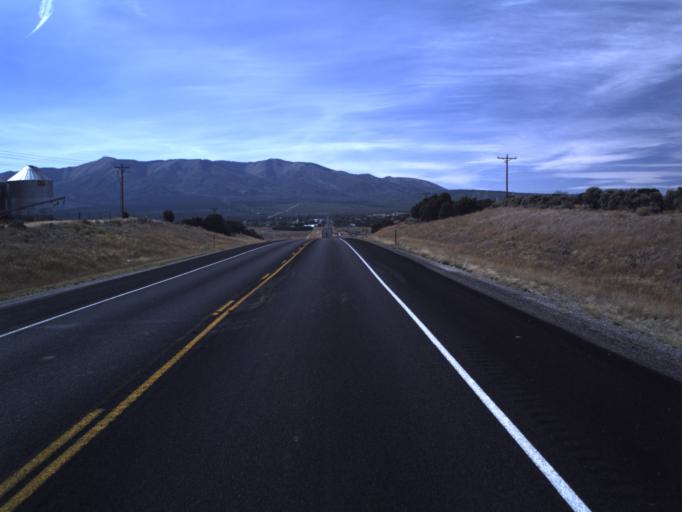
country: US
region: Utah
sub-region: San Juan County
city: Monticello
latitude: 37.8729
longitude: -109.2924
